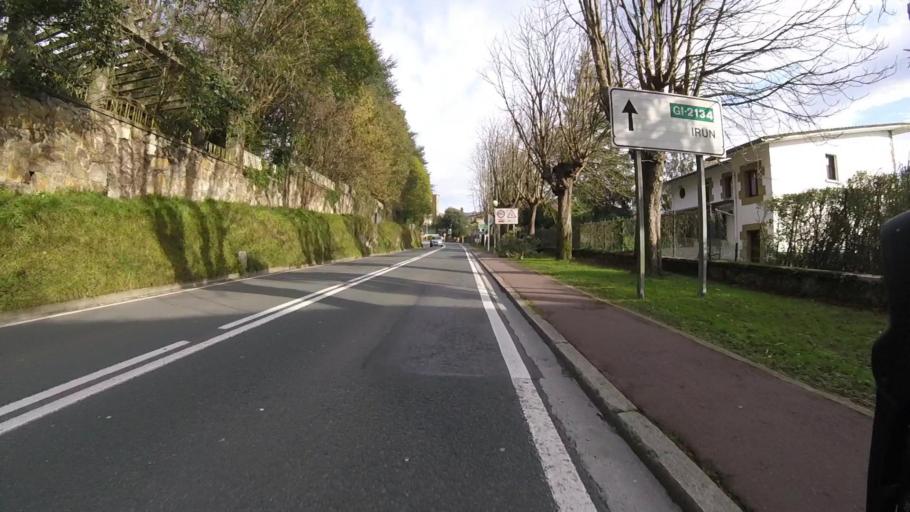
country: ES
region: Basque Country
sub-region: Provincia de Guipuzcoa
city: Lezo
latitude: 43.3003
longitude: -1.8645
